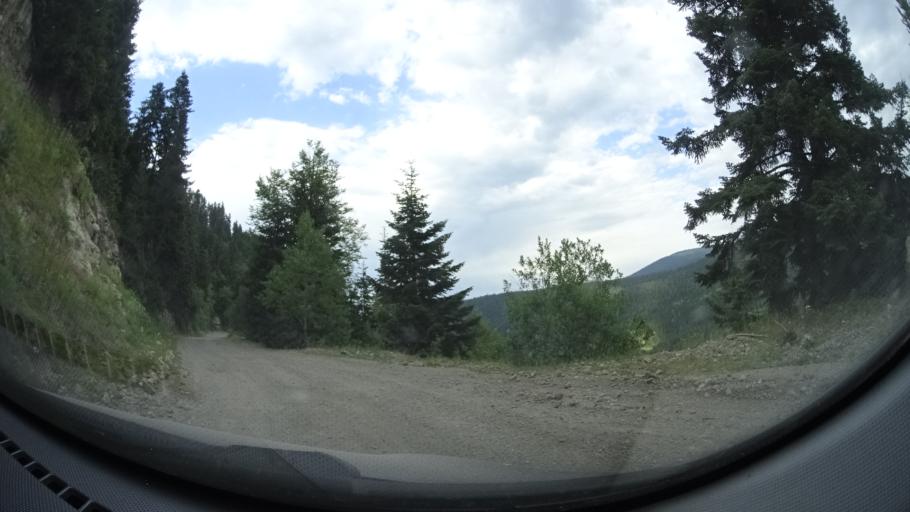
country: GE
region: Samtskhe-Javakheti
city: Adigeni
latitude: 41.6406
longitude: 42.5896
